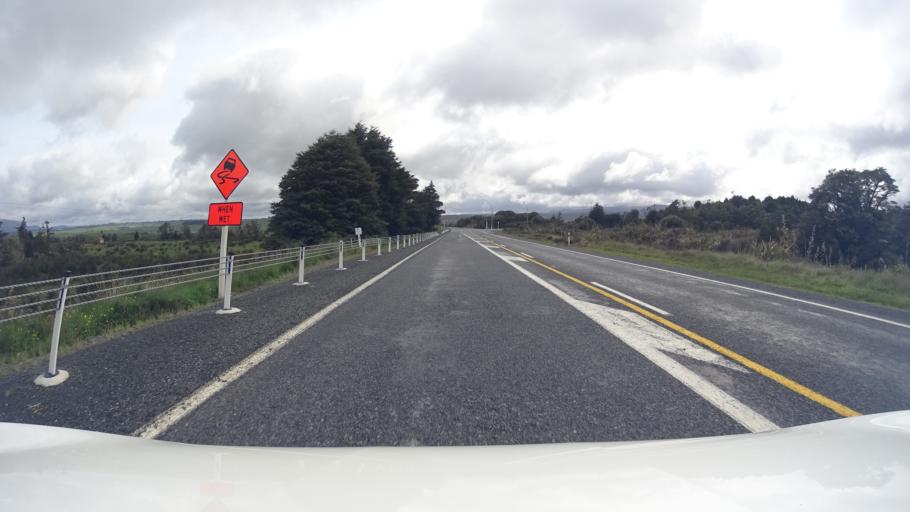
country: NZ
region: Waikato
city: Turangi
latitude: -39.1616
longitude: 175.4913
